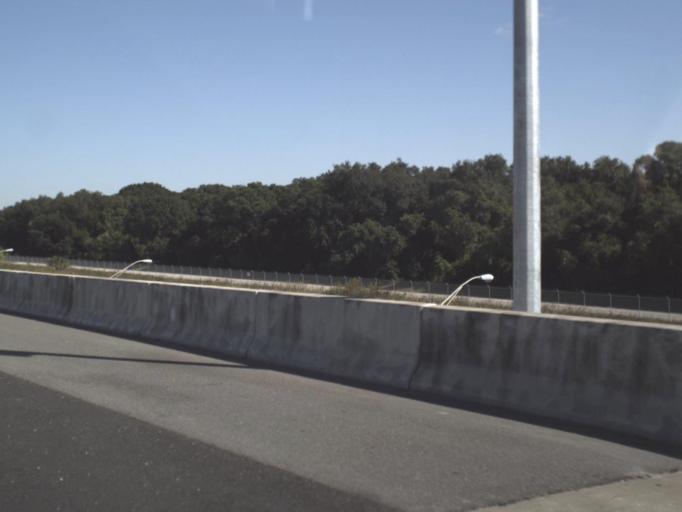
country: US
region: Florida
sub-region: Hillsborough County
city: Town 'n' Country
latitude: 27.9821
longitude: -82.5463
